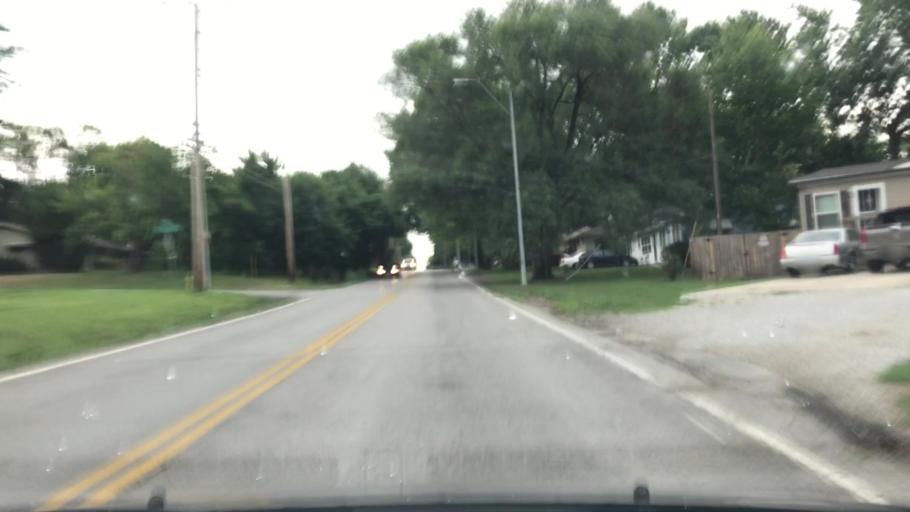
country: US
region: Missouri
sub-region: Jackson County
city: Grandview
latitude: 38.9305
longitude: -94.5053
